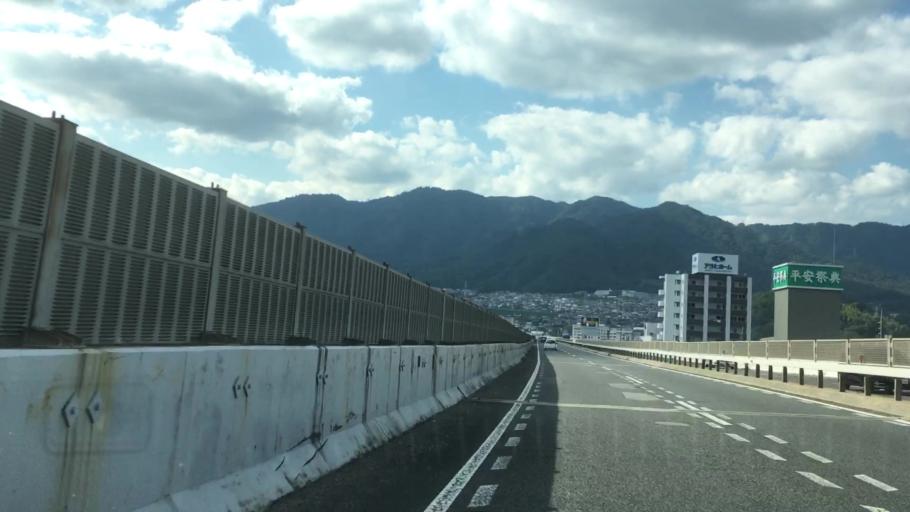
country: JP
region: Hiroshima
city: Hatsukaichi
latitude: 34.3797
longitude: 132.3623
